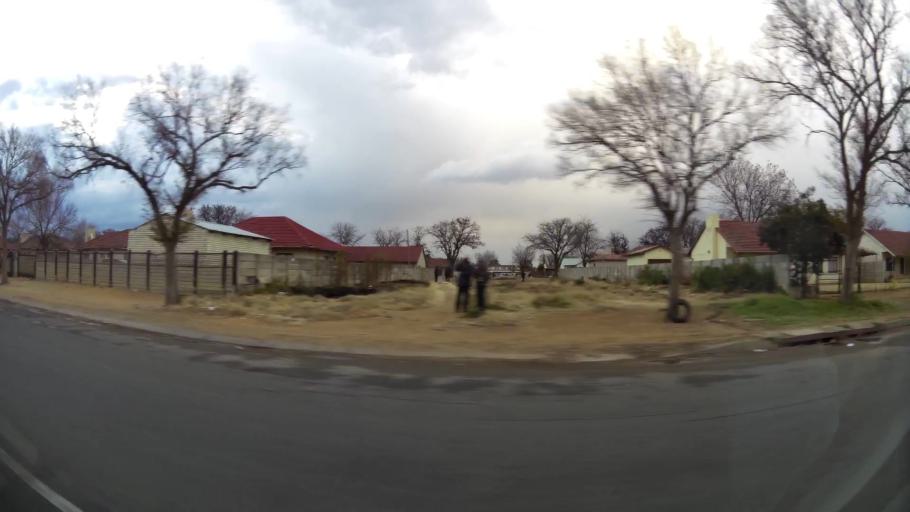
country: ZA
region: Orange Free State
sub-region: Lejweleputswa District Municipality
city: Welkom
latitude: -27.9750
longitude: 26.7685
